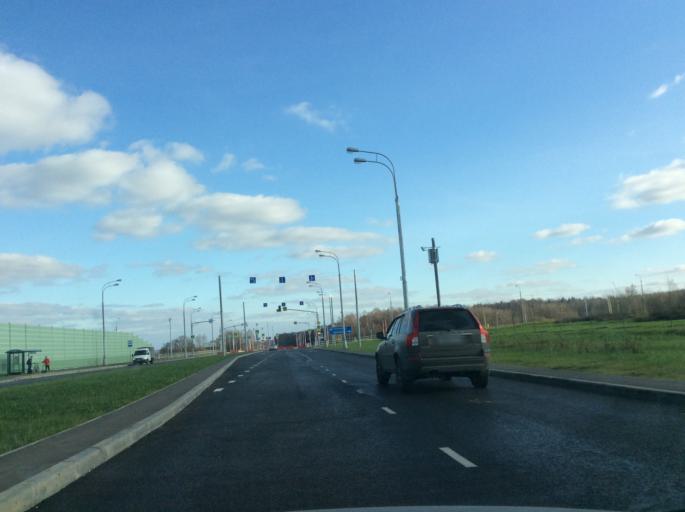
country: RU
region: Moskovskaya
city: Vatutinki
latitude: 55.4876
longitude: 37.3988
